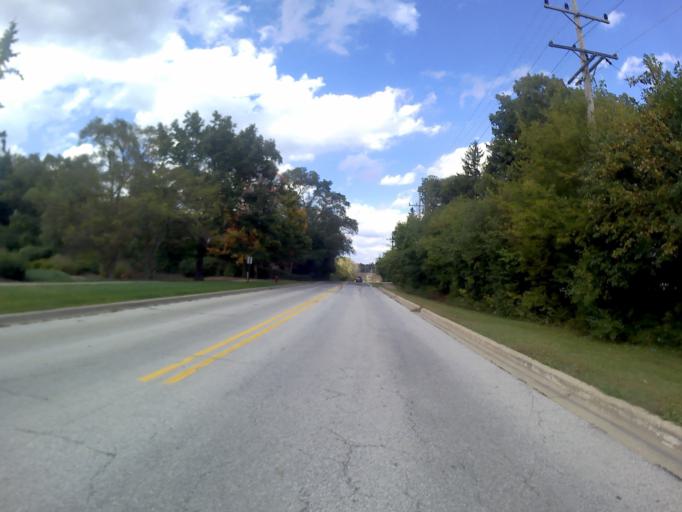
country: US
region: Illinois
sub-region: DuPage County
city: Lisle
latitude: 41.8107
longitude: -88.0938
